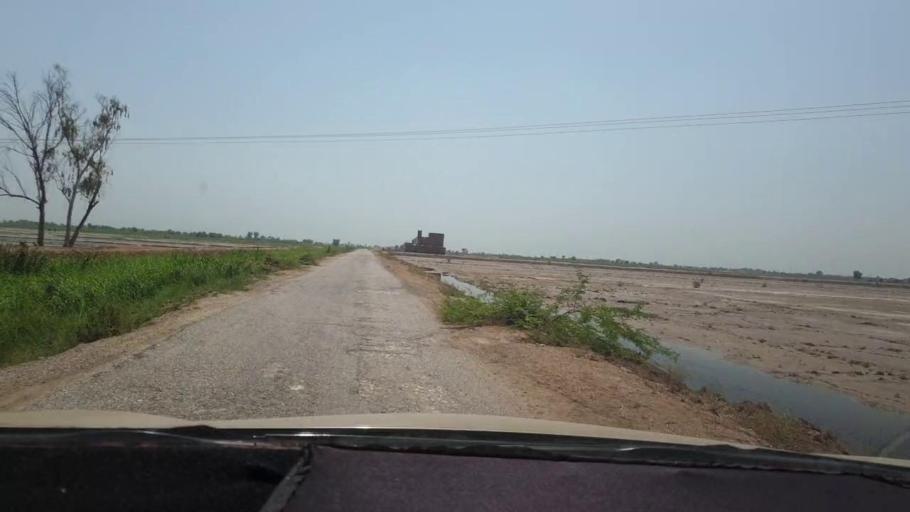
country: PK
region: Sindh
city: Shahdadkot
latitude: 27.8481
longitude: 67.9482
